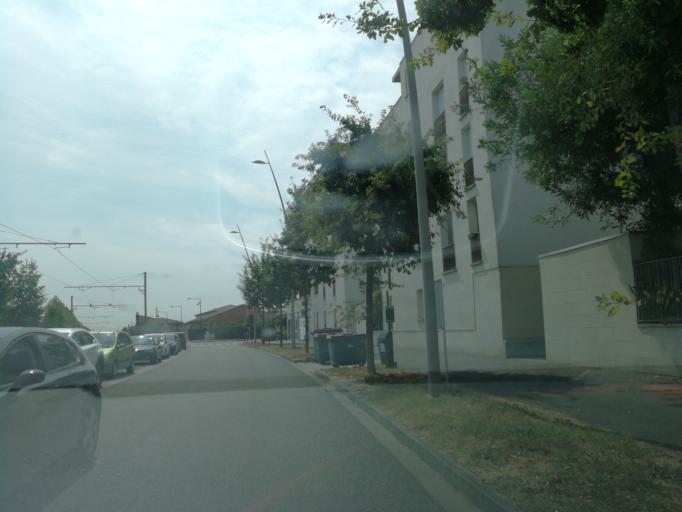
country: FR
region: Midi-Pyrenees
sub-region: Departement de la Haute-Garonne
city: Beauzelle
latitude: 43.6519
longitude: 1.3742
